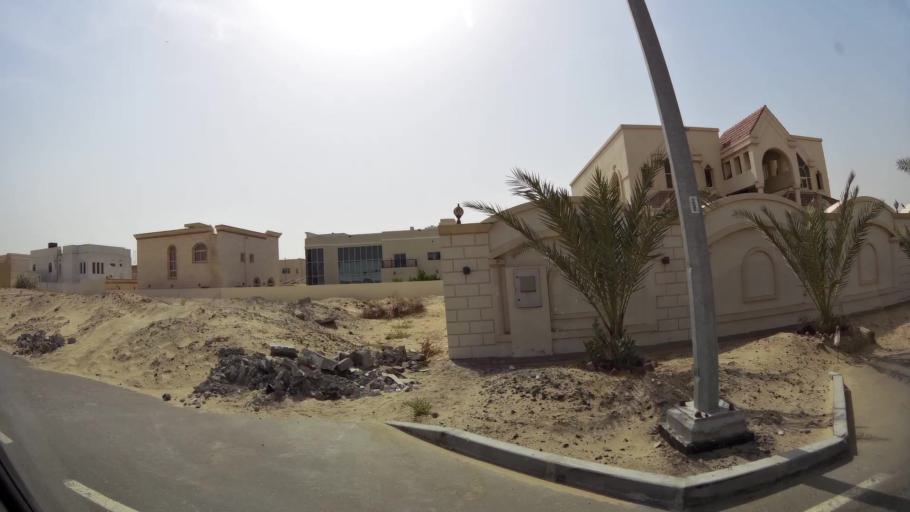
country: AE
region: Ash Shariqah
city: Sharjah
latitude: 25.2669
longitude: 55.4637
